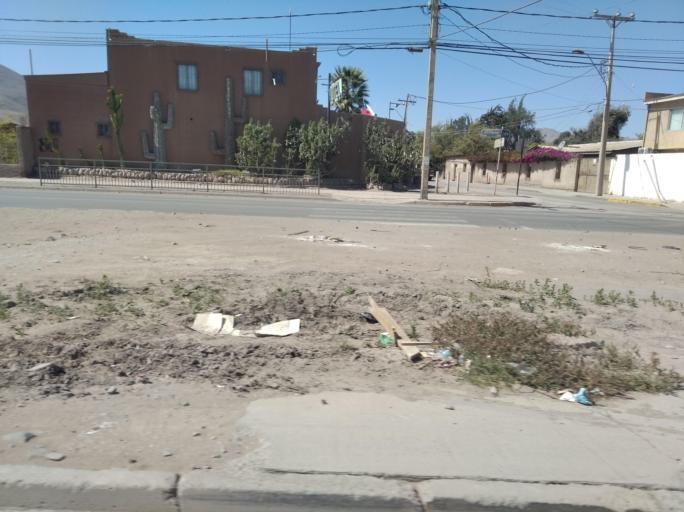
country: CL
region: Atacama
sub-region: Provincia de Copiapo
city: Copiapo
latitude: -27.4022
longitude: -70.2917
